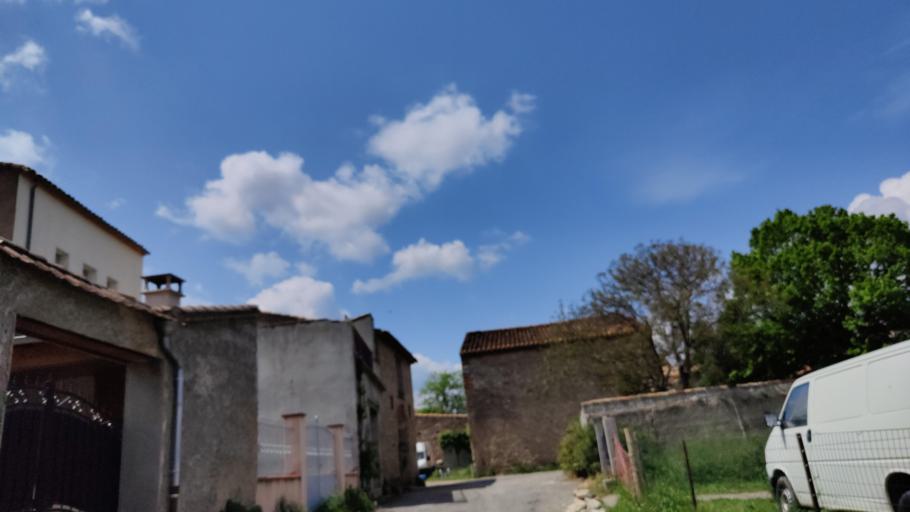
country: FR
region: Languedoc-Roussillon
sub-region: Departement des Pyrenees-Orientales
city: Estagel
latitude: 42.8590
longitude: 2.7203
